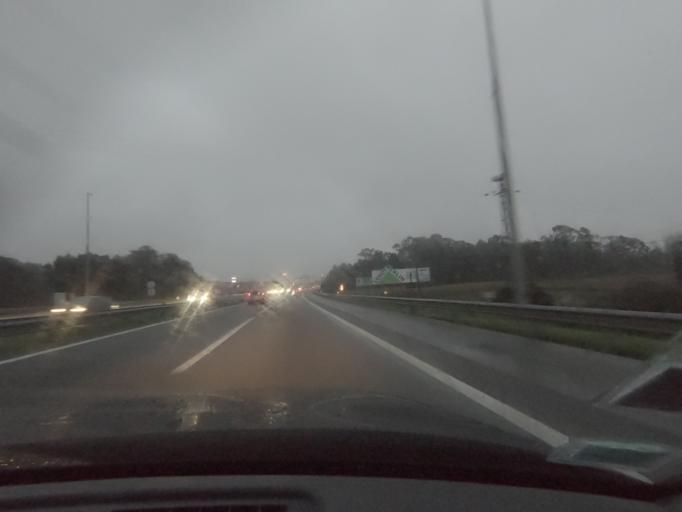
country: PT
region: Porto
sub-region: Matosinhos
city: Santa Cruz do Bispo
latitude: 41.2232
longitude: -8.6931
